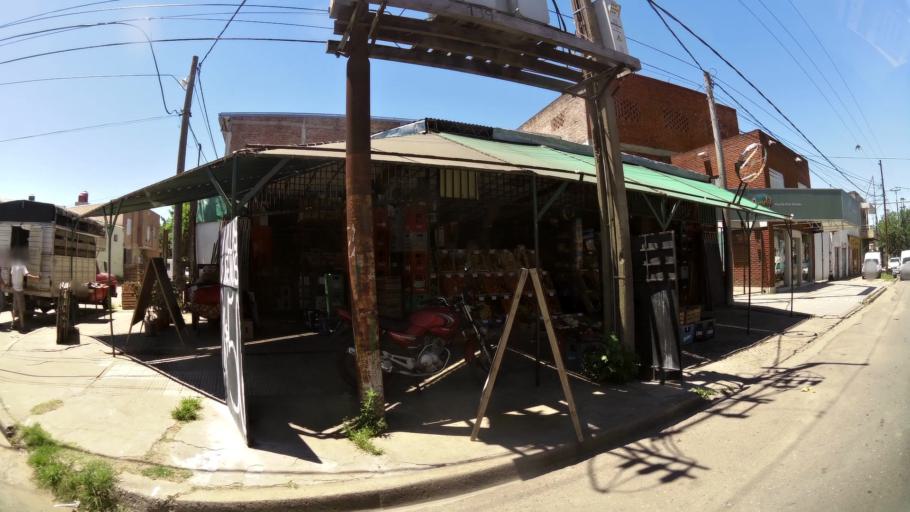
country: AR
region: Santa Fe
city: Santa Fe de la Vera Cruz
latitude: -31.6287
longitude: -60.7138
